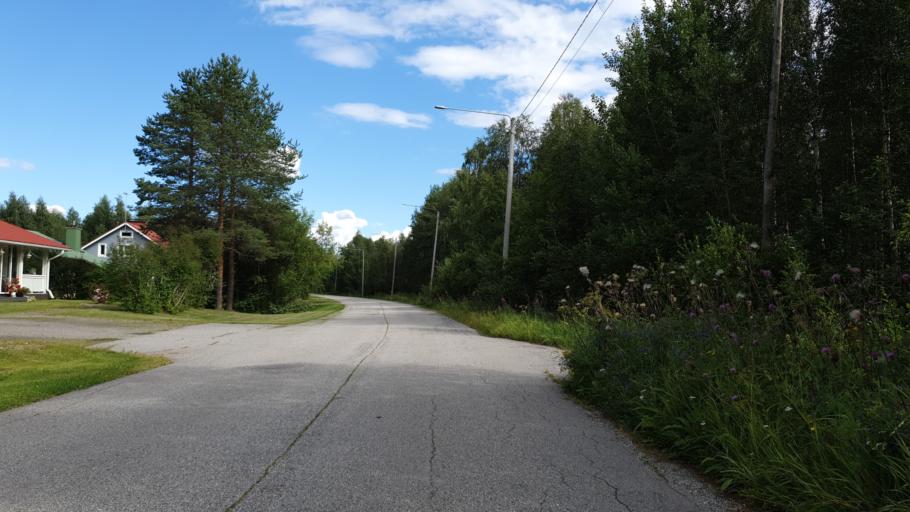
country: FI
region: Kainuu
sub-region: Kehys-Kainuu
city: Kuhmo
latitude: 64.1186
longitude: 29.5627
